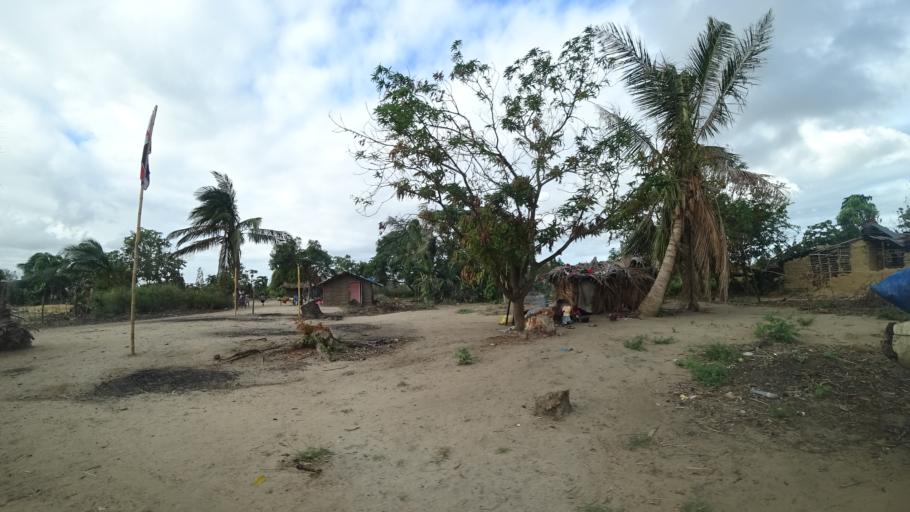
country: MZ
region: Sofala
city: Beira
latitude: -19.6558
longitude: 35.0610
